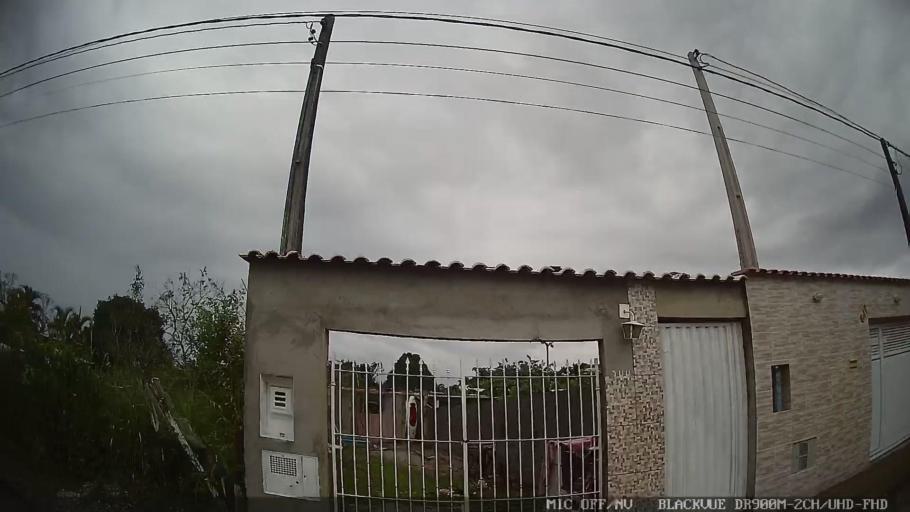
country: BR
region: Sao Paulo
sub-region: Itanhaem
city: Itanhaem
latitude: -24.1592
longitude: -46.8008
